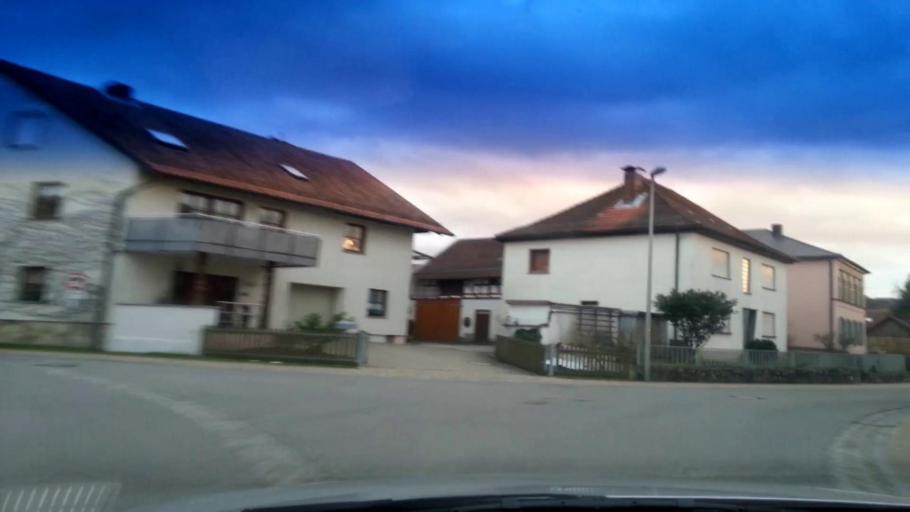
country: DE
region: Bavaria
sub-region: Upper Franconia
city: Schesslitz
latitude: 49.9715
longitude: 11.0584
